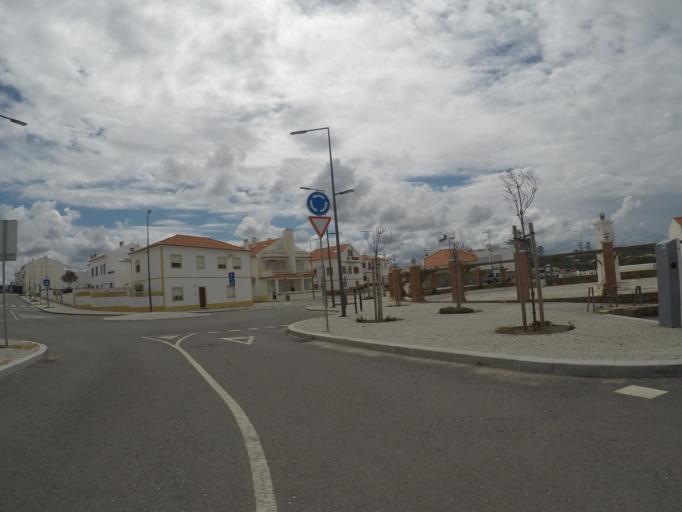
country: PT
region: Beja
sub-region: Odemira
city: Sao Teotonio
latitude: 37.5252
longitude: -8.7869
